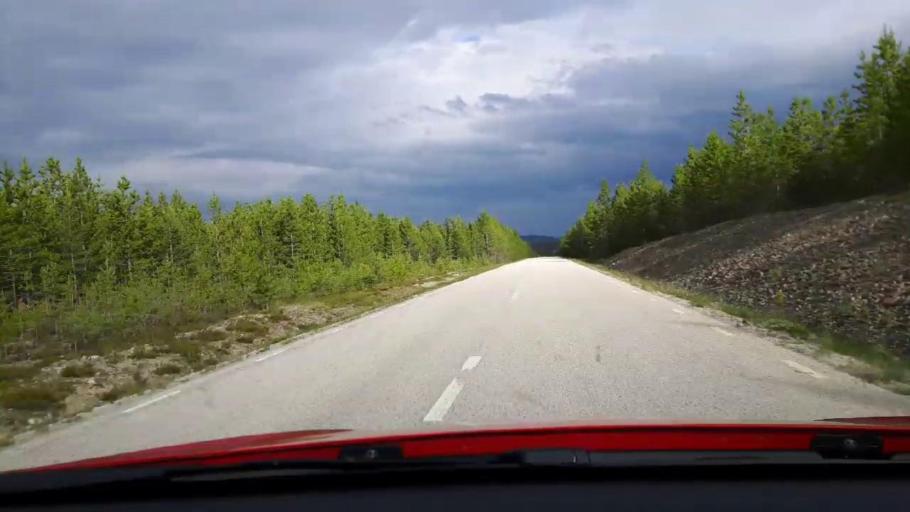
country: SE
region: Jaemtland
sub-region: Bergs Kommun
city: Hoverberg
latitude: 62.6725
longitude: 14.0251
